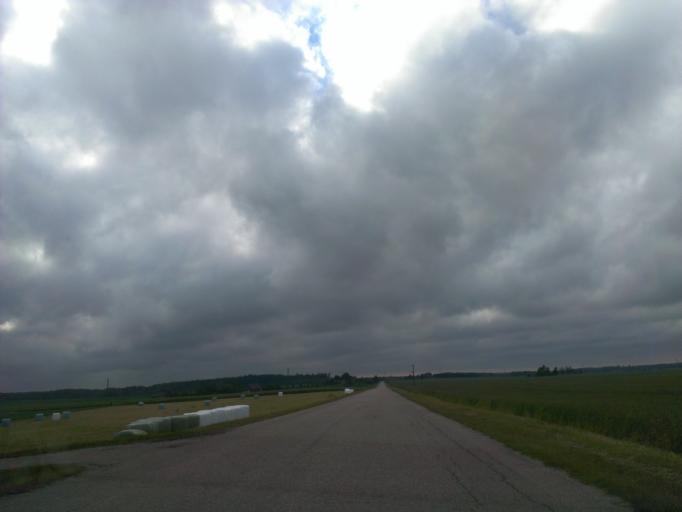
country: LV
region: Aizpute
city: Aizpute
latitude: 56.7138
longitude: 21.4723
